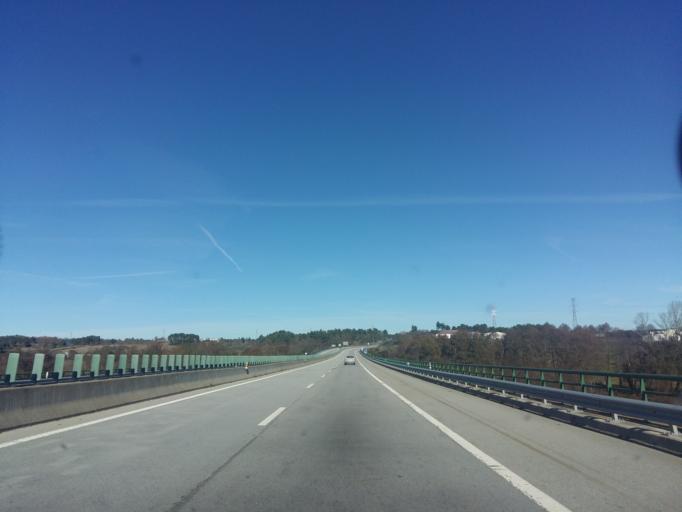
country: PT
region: Guarda
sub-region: Guarda
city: Guarda
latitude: 40.5145
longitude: -7.2332
